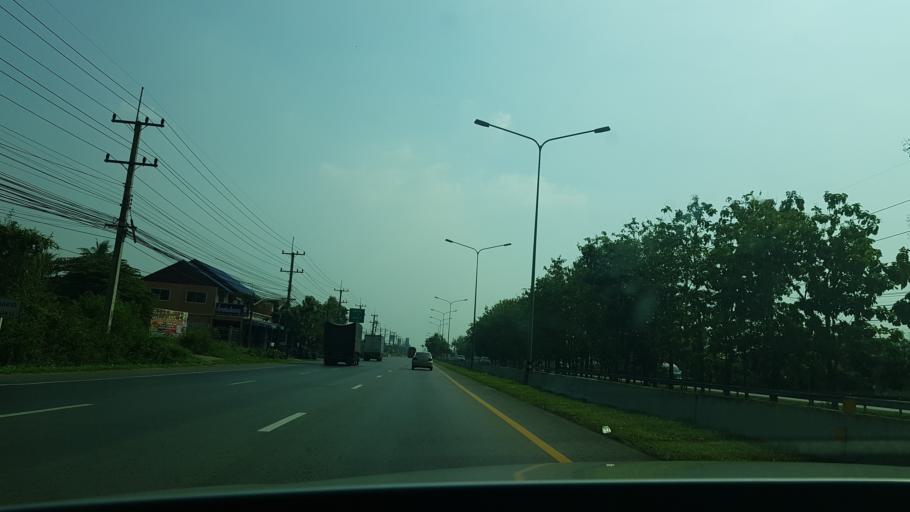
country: TH
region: Ratchaburi
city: Pak Tho
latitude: 13.3148
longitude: 99.8268
